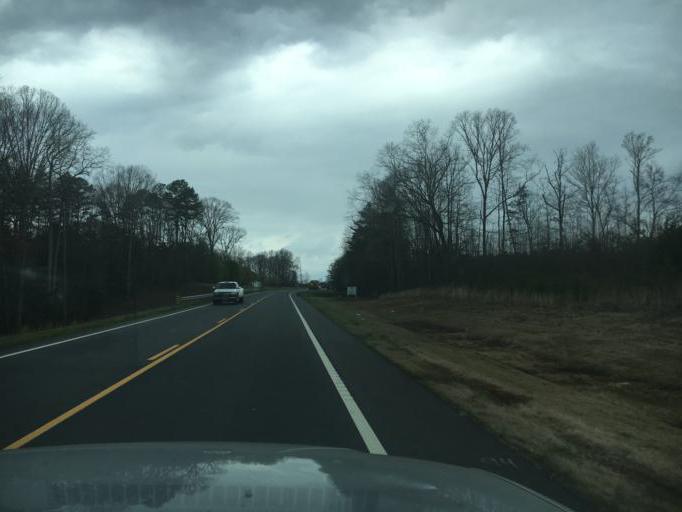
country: US
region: South Carolina
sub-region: Oconee County
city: Walhalla
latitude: 34.7977
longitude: -83.0283
